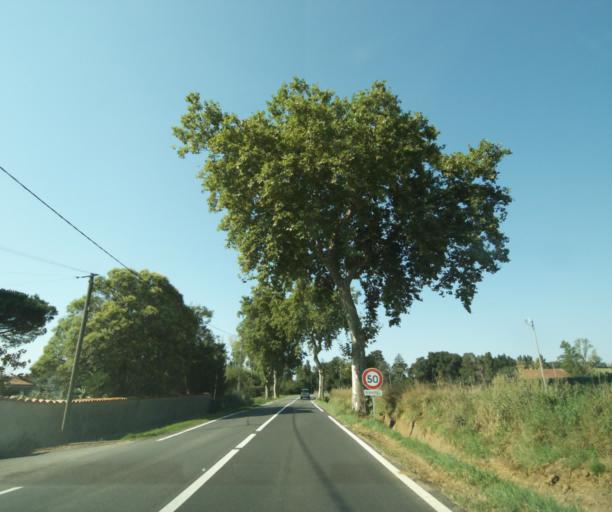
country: FR
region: Midi-Pyrenees
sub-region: Departement de la Haute-Garonne
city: Beaumont-sur-Leze
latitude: 43.3882
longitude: 1.3497
